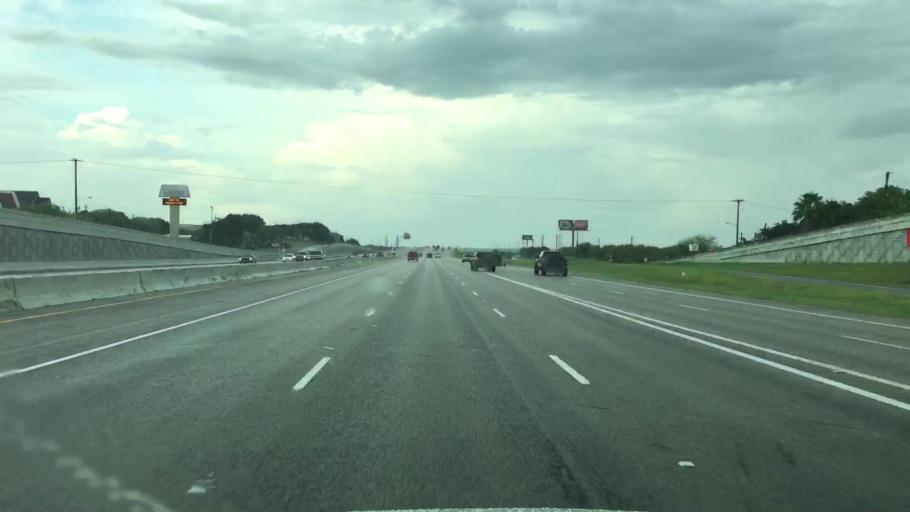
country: US
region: Texas
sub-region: Nueces County
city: Robstown
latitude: 27.8681
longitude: -97.6230
